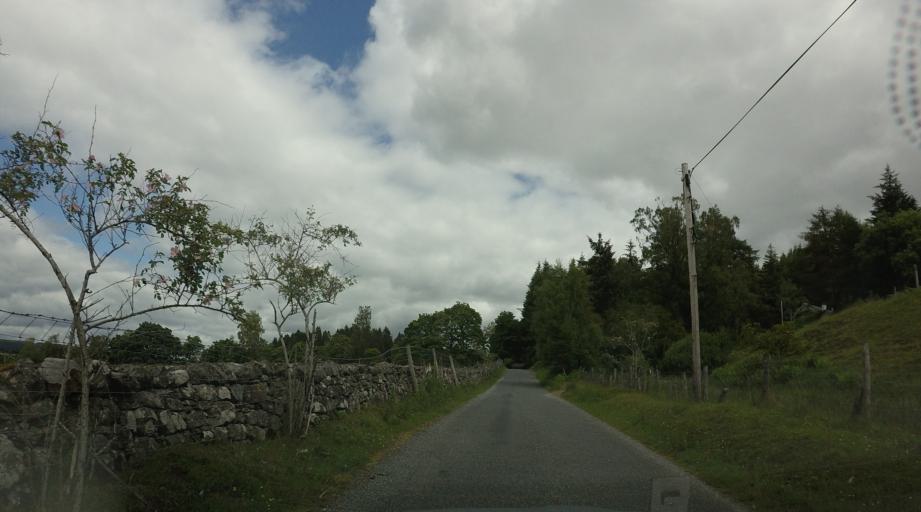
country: GB
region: Scotland
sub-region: Perth and Kinross
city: Aberfeldy
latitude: 56.6931
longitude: -4.1262
